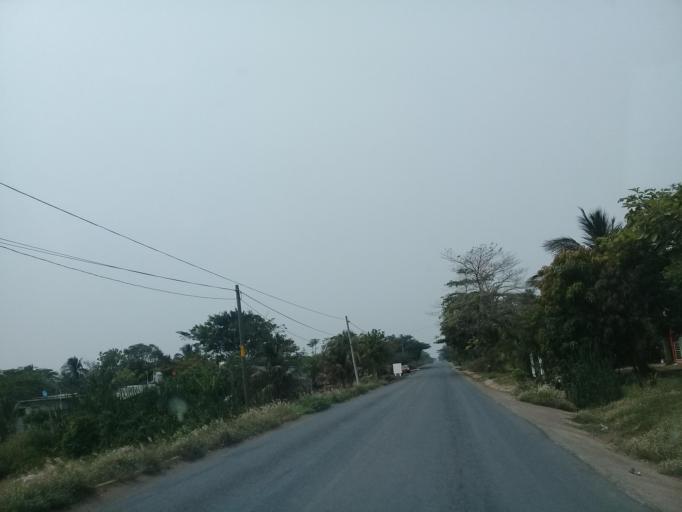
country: MX
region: Veracruz
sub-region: Medellin
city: La Laguna y Monte del Castillo
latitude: 18.9811
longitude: -96.1181
